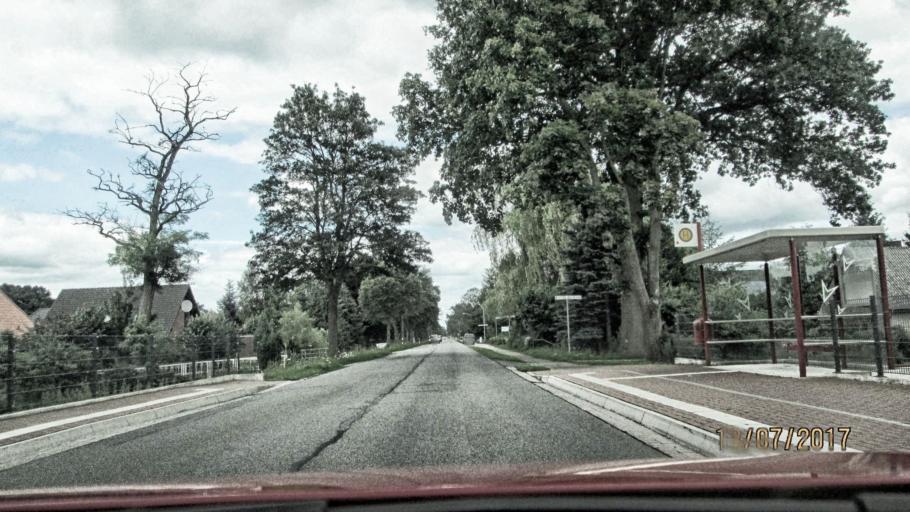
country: DE
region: Lower Saxony
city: Sassenburg
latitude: 52.5168
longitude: 10.5863
